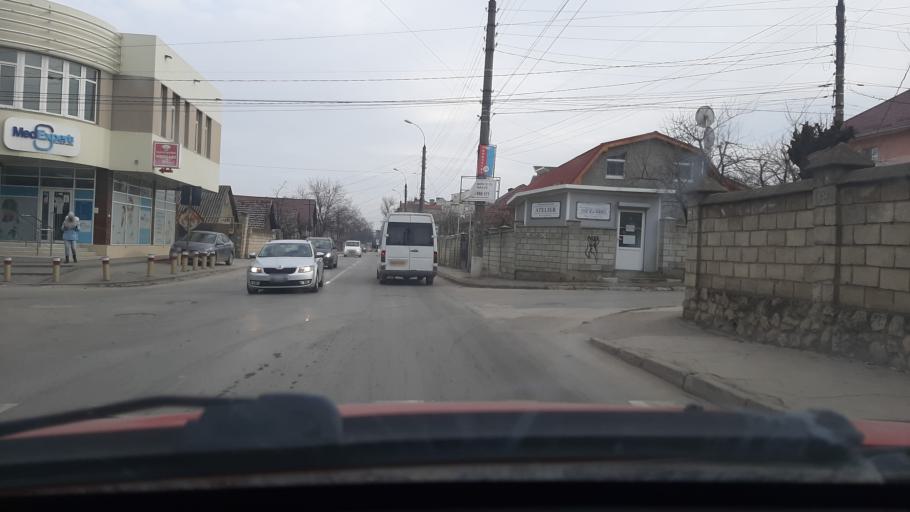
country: MD
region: Chisinau
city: Vatra
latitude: 47.0347
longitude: 28.7892
